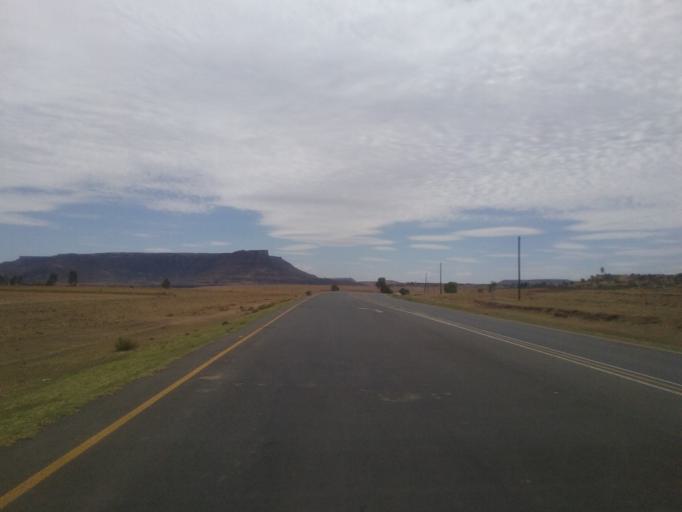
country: LS
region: Mafeteng
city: Mafeteng
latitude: -29.6808
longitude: 27.4452
